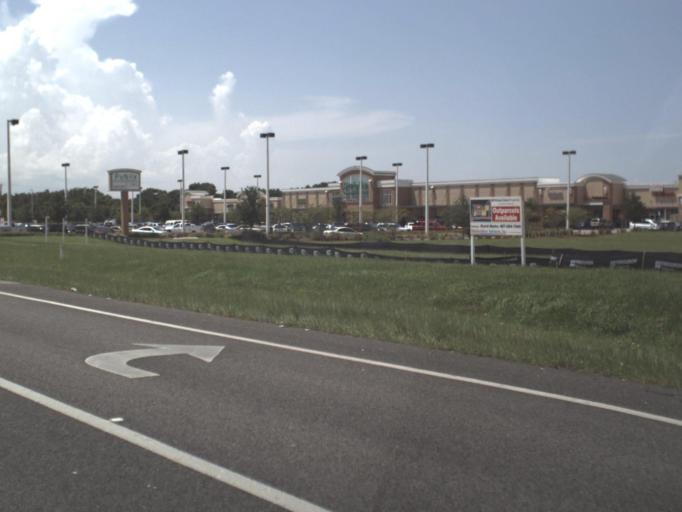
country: US
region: Florida
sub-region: Hillsborough County
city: Progress Village
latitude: 27.9146
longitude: -82.3487
